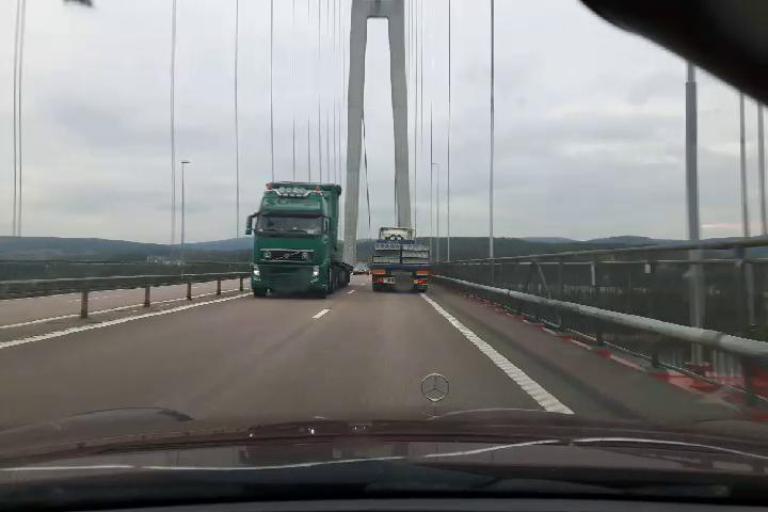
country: SE
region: Vaesternorrland
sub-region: Haernoesands Kommun
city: Haernoesand
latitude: 62.7933
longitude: 17.9306
